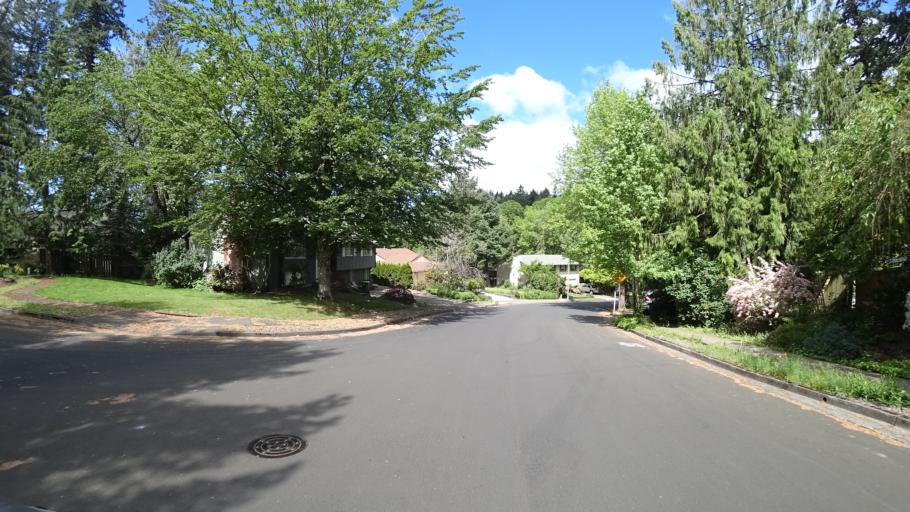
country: US
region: Oregon
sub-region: Washington County
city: Beaverton
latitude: 45.4711
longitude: -122.8093
